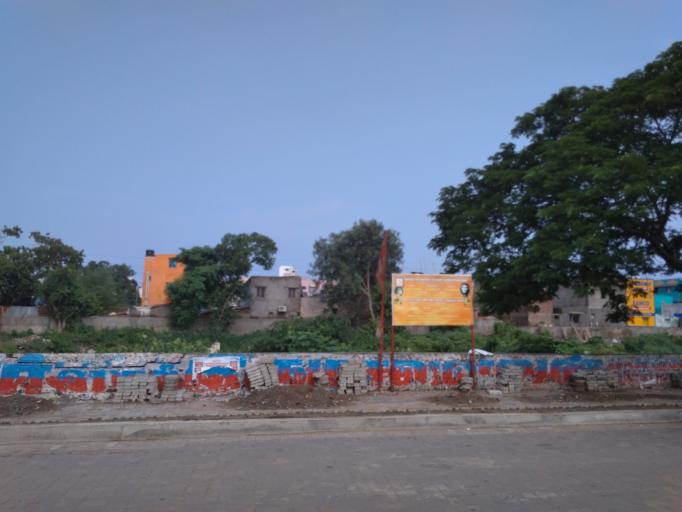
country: IN
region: Tamil Nadu
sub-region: Kancheepuram
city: Perungudi
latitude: 12.9791
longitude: 80.2528
